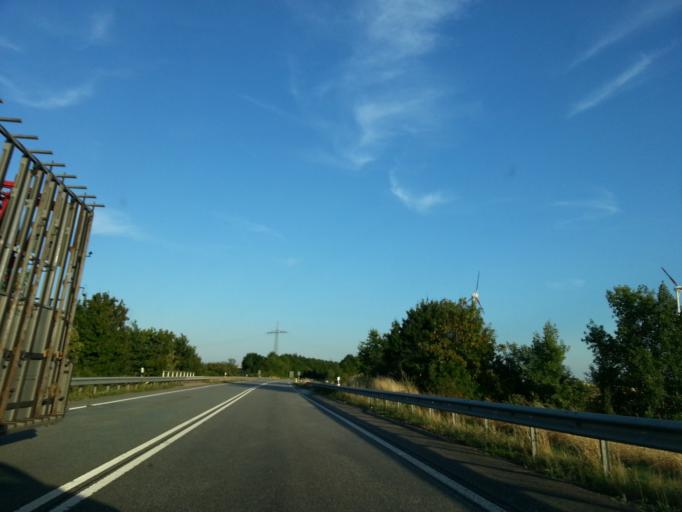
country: DE
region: Rheinland-Pfalz
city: Weselberg
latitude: 49.3284
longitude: 7.6094
